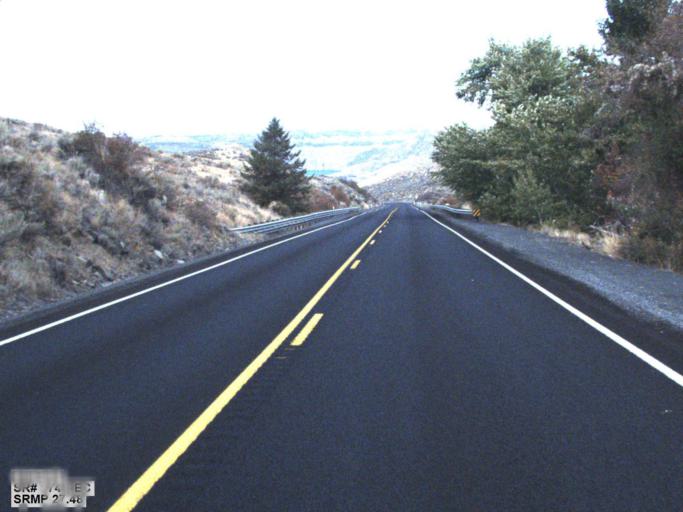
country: US
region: Washington
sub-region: Okanogan County
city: Coulee Dam
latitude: 47.9159
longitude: -118.8987
